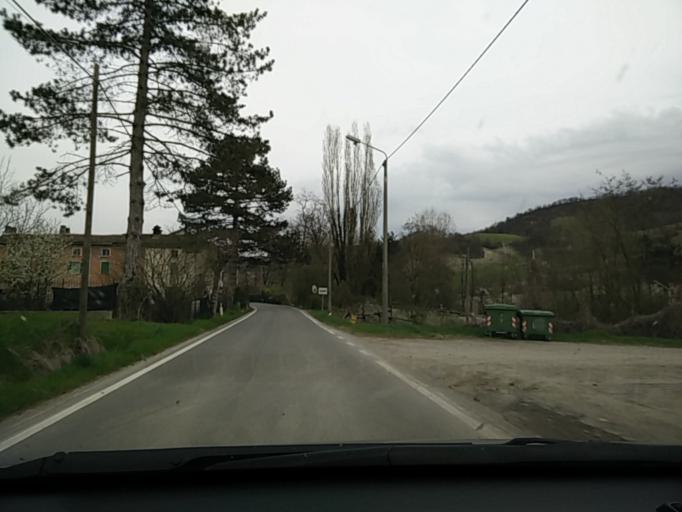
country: IT
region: Lombardy
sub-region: Provincia di Pavia
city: Susella
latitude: 44.8959
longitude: 9.0824
